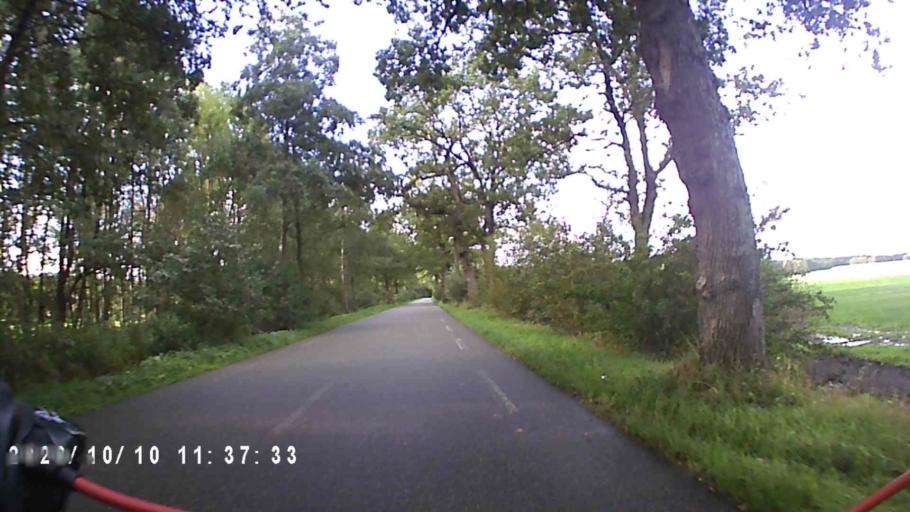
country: NL
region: Friesland
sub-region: Gemeente Smallingerland
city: Drachten
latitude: 53.0730
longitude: 6.1138
